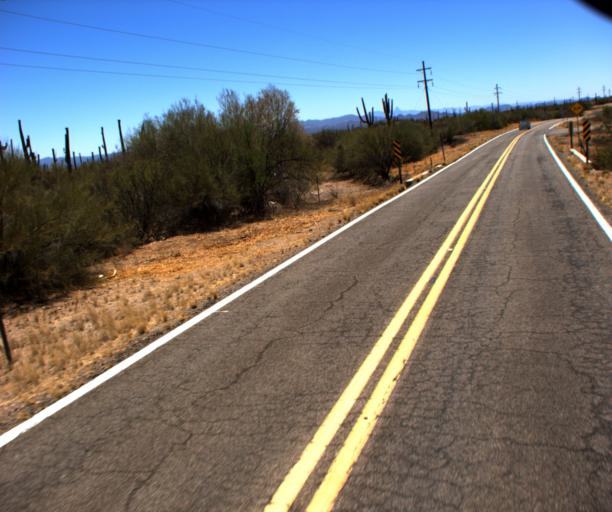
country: US
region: Arizona
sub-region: Pima County
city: Sells
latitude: 32.1571
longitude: -112.1090
